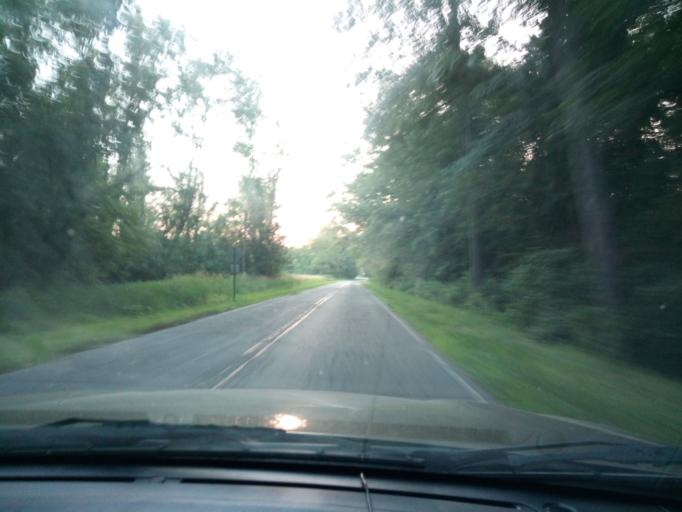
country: US
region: New York
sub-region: Wayne County
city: Clyde
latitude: 43.0209
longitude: -76.8010
